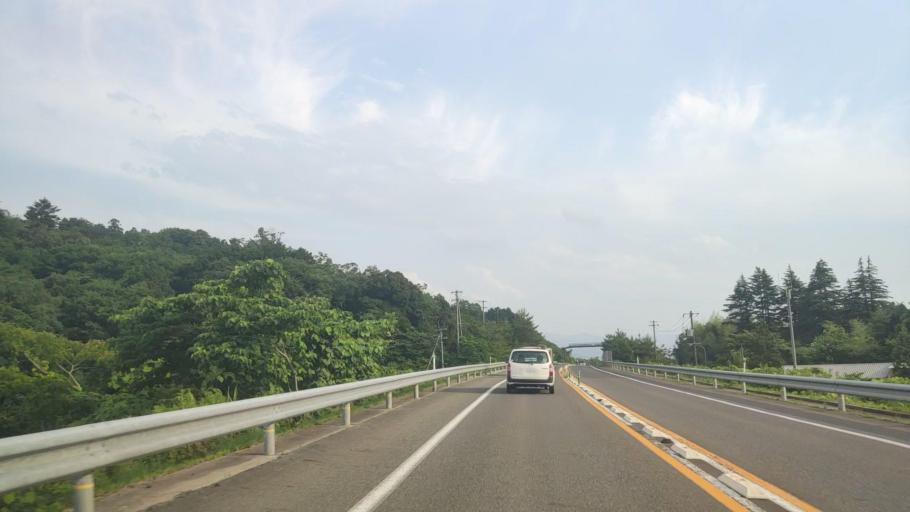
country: JP
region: Tottori
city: Kurayoshi
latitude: 35.4553
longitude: 133.8107
